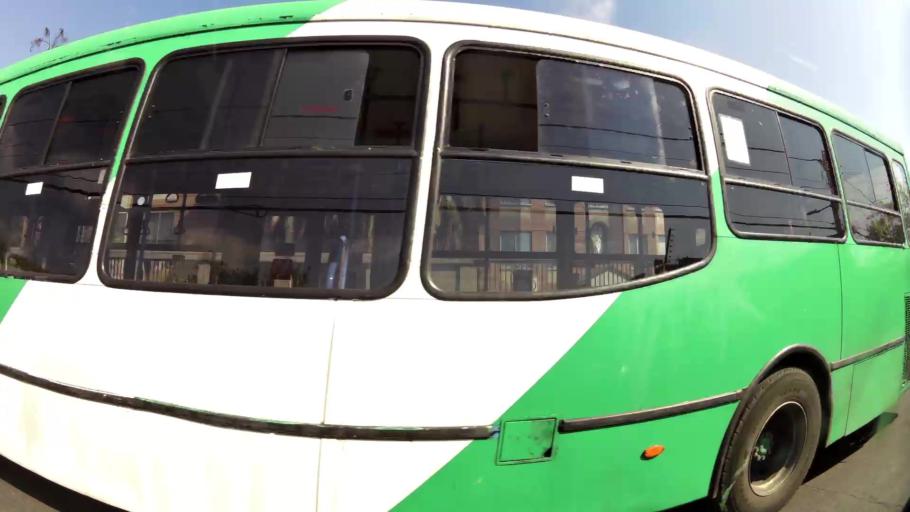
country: CL
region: Santiago Metropolitan
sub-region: Provincia de Maipo
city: San Bernardo
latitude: -33.5961
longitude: -70.6949
